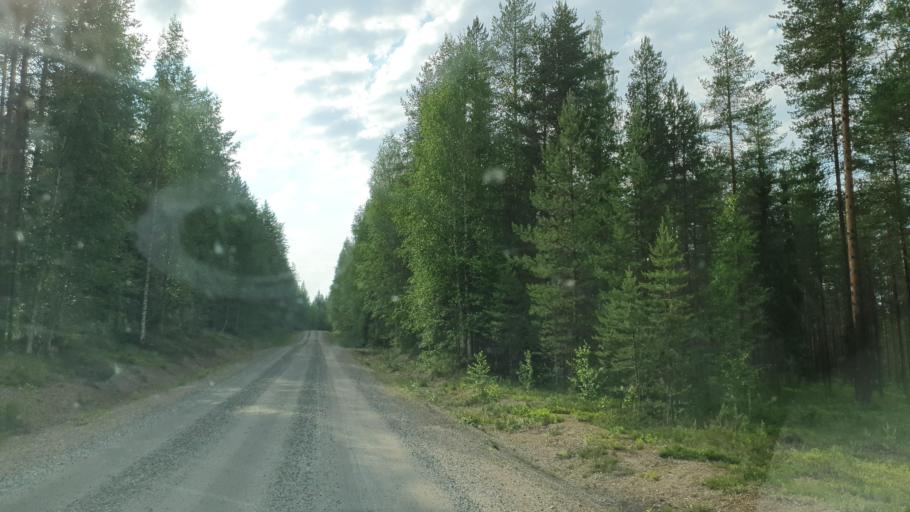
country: FI
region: Kainuu
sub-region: Kehys-Kainuu
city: Kuhmo
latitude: 64.0601
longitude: 29.7665
